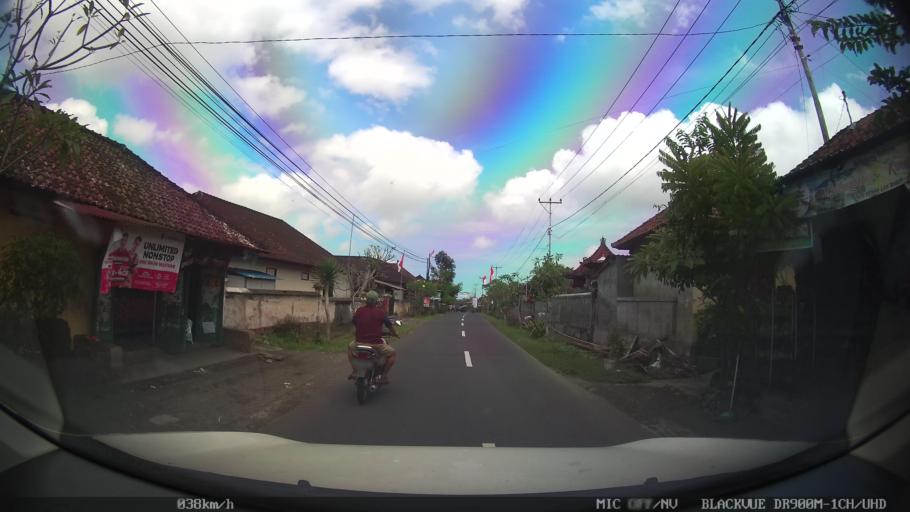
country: ID
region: Bali
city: Klungkung
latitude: -8.5234
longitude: 115.3809
